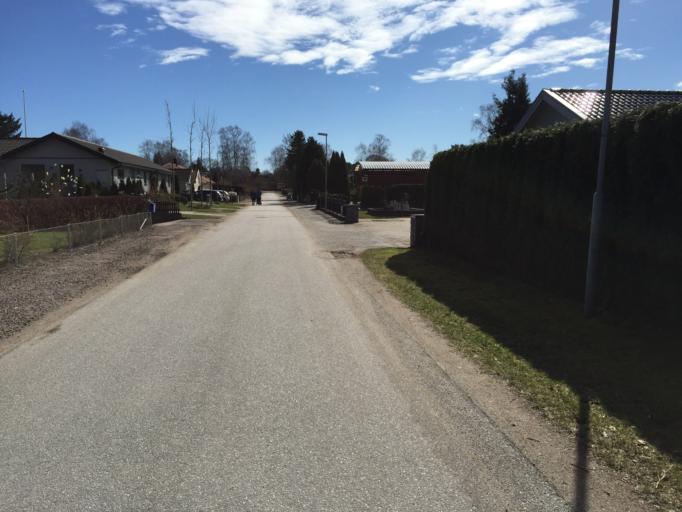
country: SE
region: Skane
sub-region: Lunds Kommun
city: Veberod
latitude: 55.6322
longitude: 13.5040
